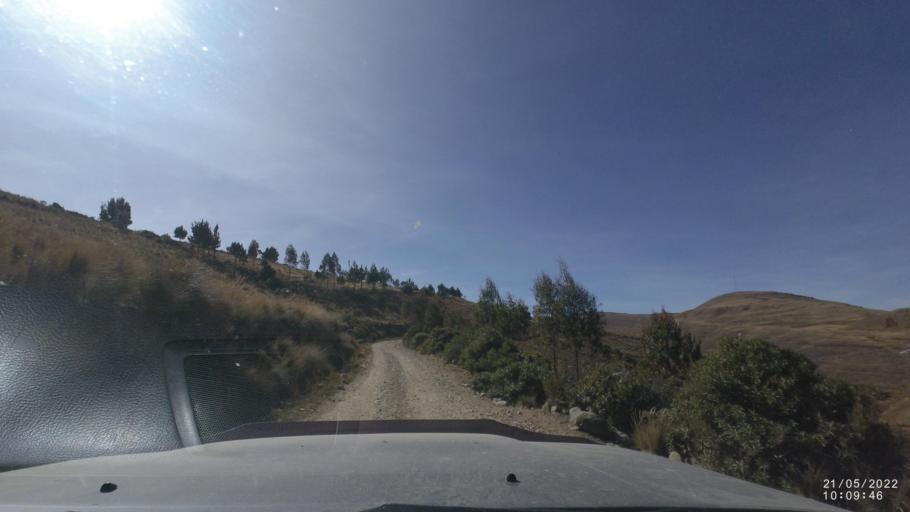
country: BO
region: Cochabamba
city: Colomi
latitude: -17.3363
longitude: -65.9852
